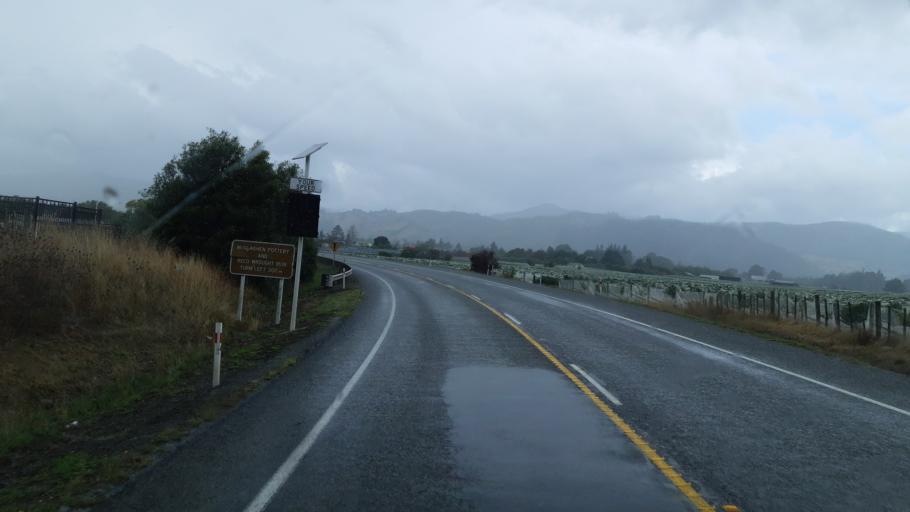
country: NZ
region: Tasman
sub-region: Tasman District
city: Brightwater
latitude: -41.3798
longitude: 173.1095
